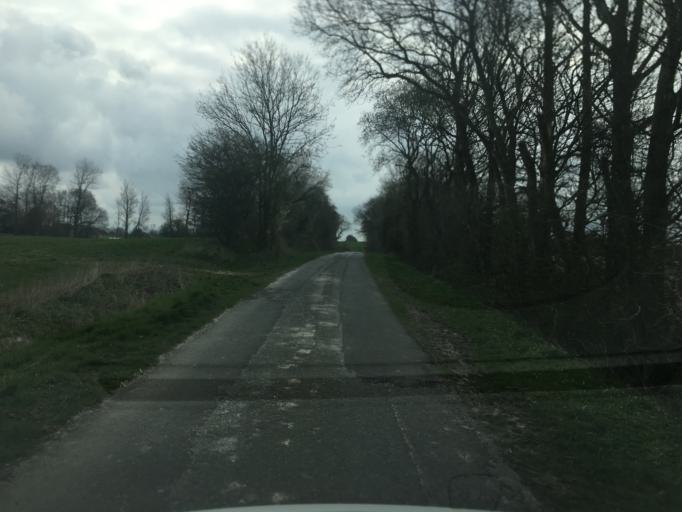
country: DE
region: Schleswig-Holstein
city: Glucksburg
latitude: 54.9008
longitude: 9.5113
